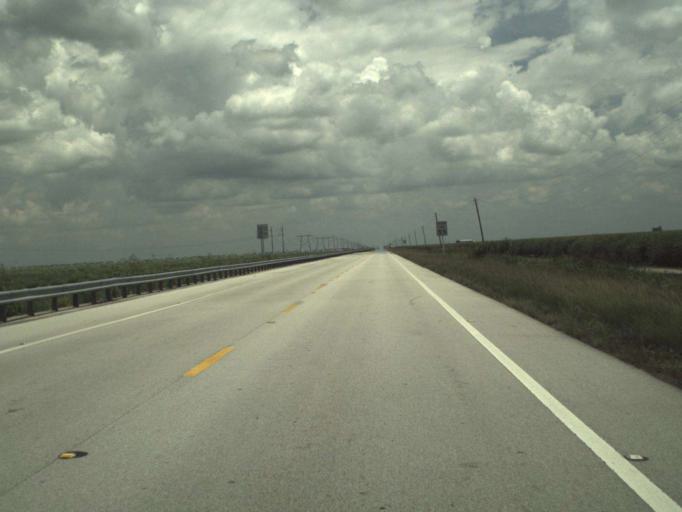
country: US
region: Florida
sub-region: Palm Beach County
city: Pahokee
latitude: 26.8332
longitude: -80.5904
